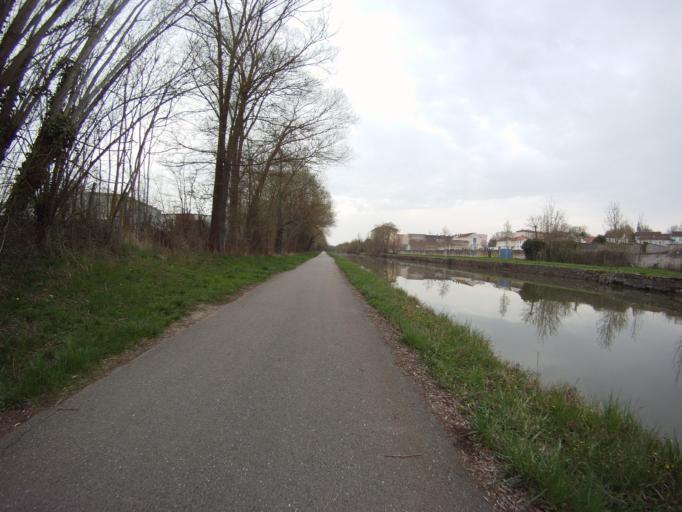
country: FR
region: Lorraine
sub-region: Departement de Meurthe-et-Moselle
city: Jarville-la-Malgrange
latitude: 48.6675
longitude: 6.2141
